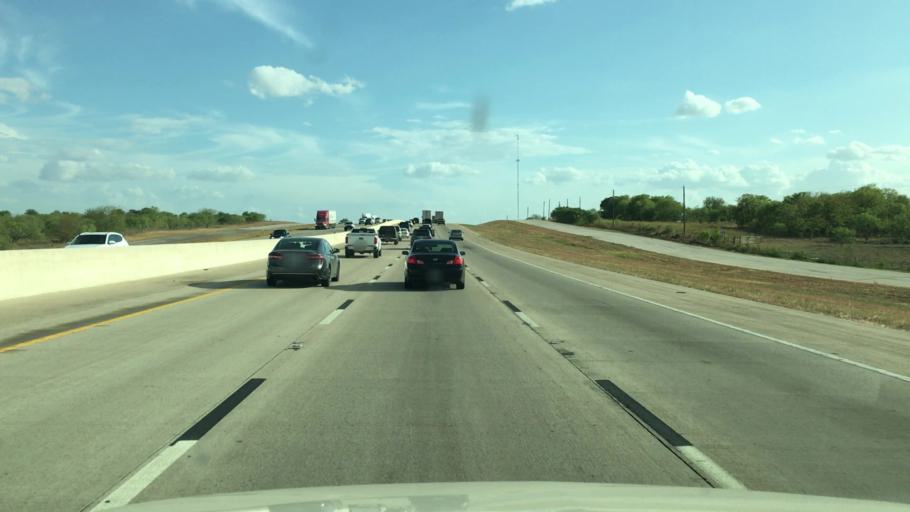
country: US
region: Texas
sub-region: Bell County
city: Salado
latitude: 30.8679
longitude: -97.5843
